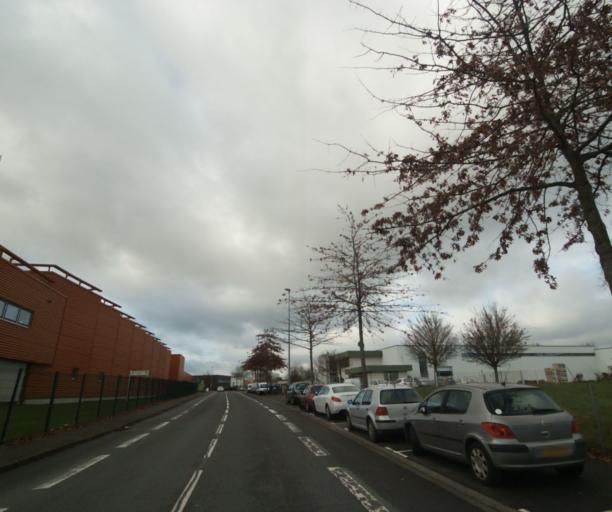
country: FR
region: Pays de la Loire
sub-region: Departement de la Sarthe
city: Rouillon
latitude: 48.0116
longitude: 0.1576
